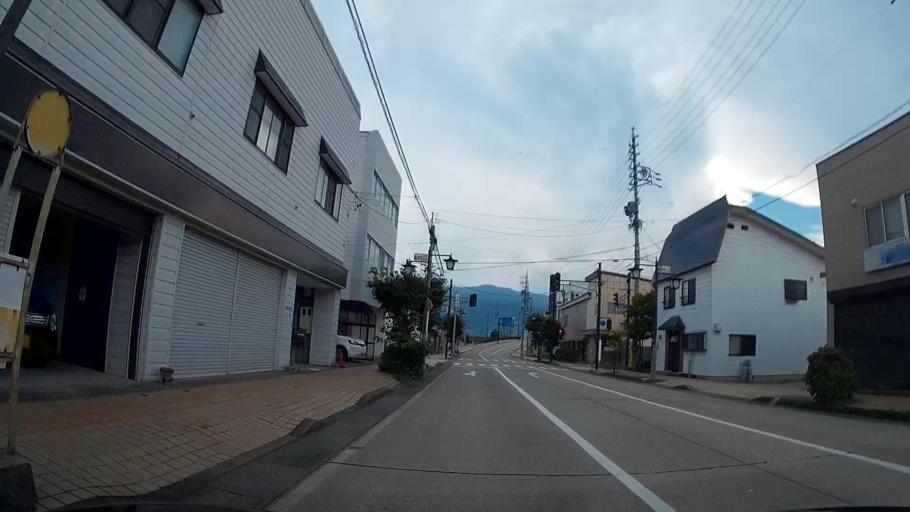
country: JP
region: Nagano
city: Iiyama
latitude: 36.8534
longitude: 138.3645
